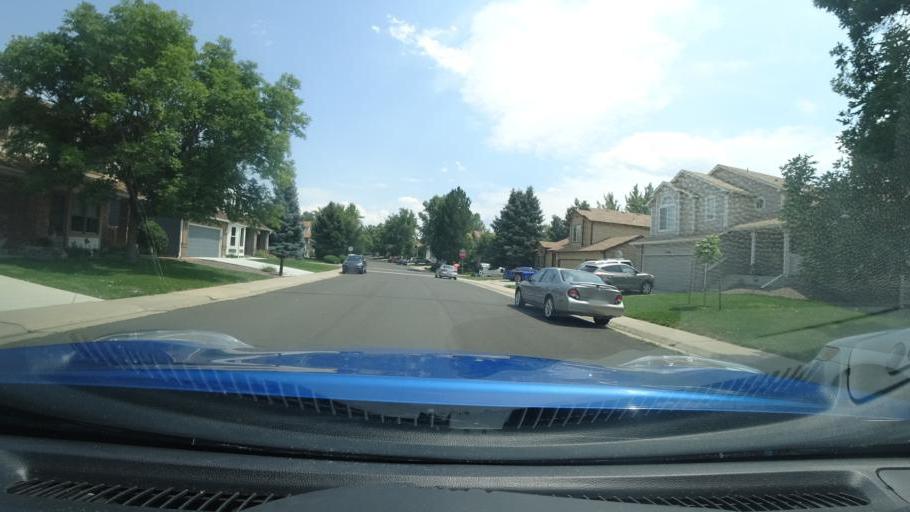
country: US
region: Colorado
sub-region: Adams County
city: Aurora
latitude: 39.6710
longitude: -104.7821
